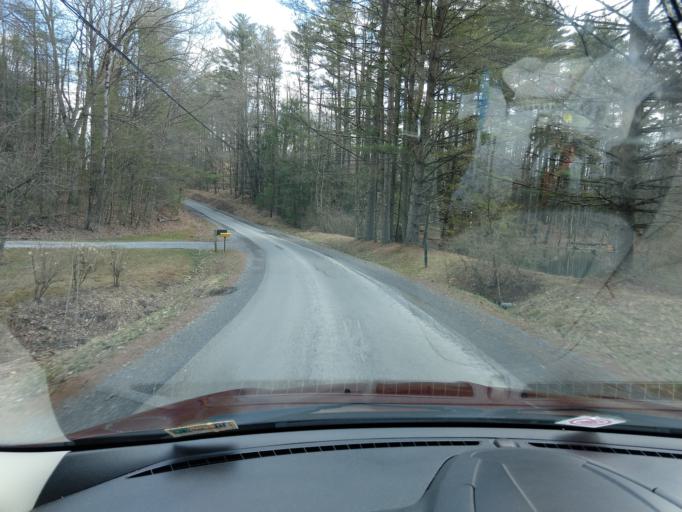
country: US
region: West Virginia
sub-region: Greenbrier County
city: Fairlea
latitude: 37.8263
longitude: -80.5222
